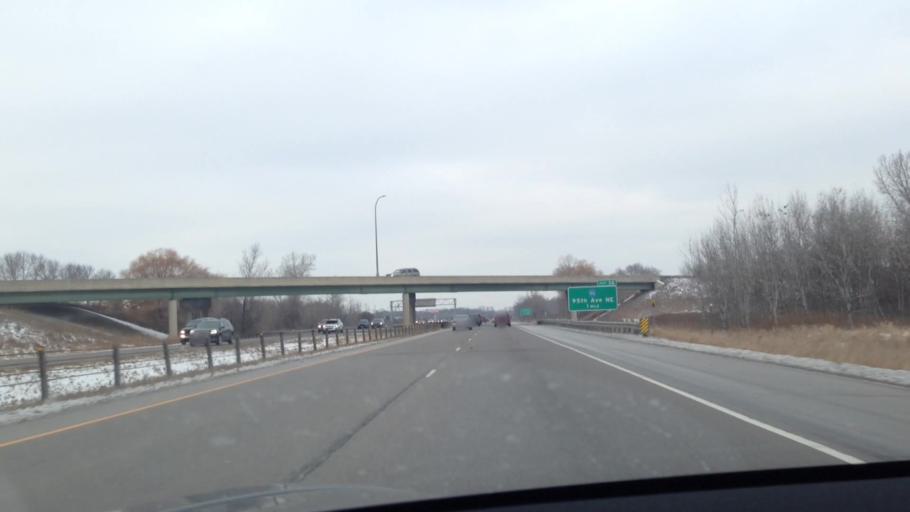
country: US
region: Minnesota
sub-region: Anoka County
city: Lexington
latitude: 45.1270
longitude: -93.1884
